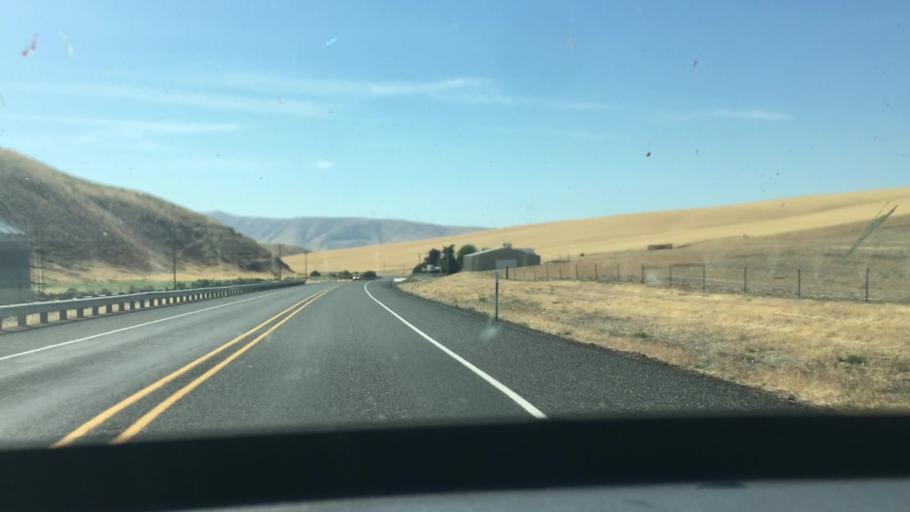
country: US
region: Oregon
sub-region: Sherman County
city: Moro
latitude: 45.6322
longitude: -120.7632
